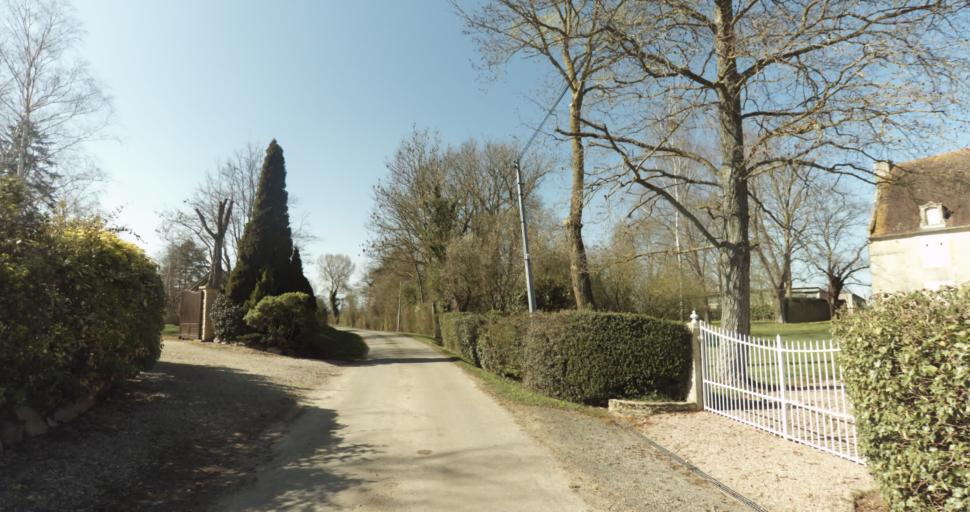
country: FR
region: Lower Normandy
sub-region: Departement du Calvados
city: Saint-Pierre-sur-Dives
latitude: 48.9471
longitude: -0.0060
